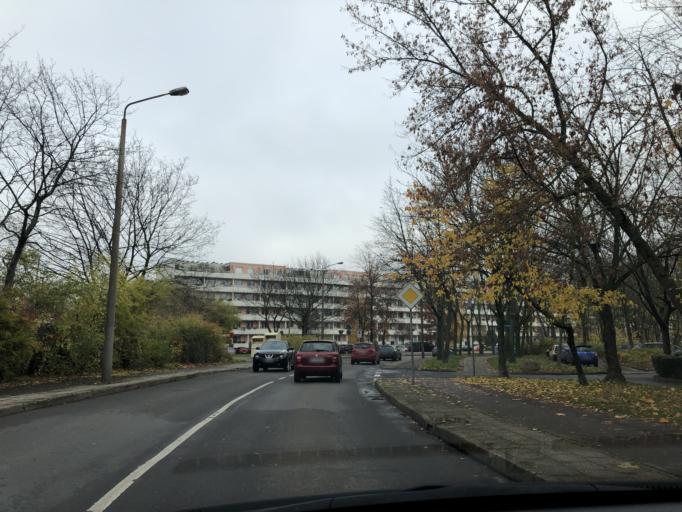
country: DE
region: Saxony-Anhalt
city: Halle Neustadt
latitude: 51.4832
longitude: 11.9349
